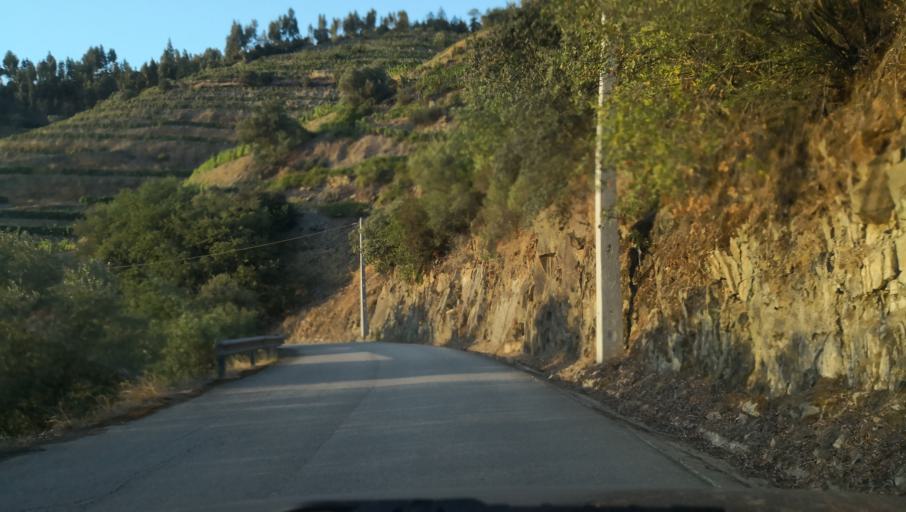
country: PT
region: Viseu
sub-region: Armamar
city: Armamar
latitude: 41.1363
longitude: -7.6925
